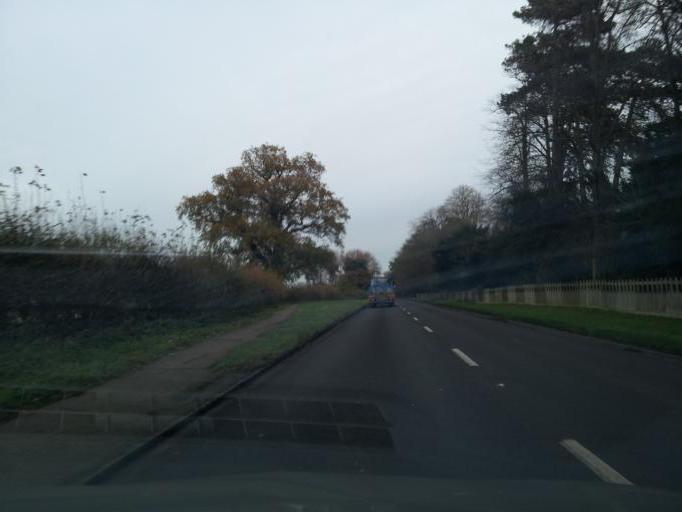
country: GB
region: England
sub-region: Central Bedfordshire
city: Leighton Buzzard
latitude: 51.9014
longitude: -0.7020
